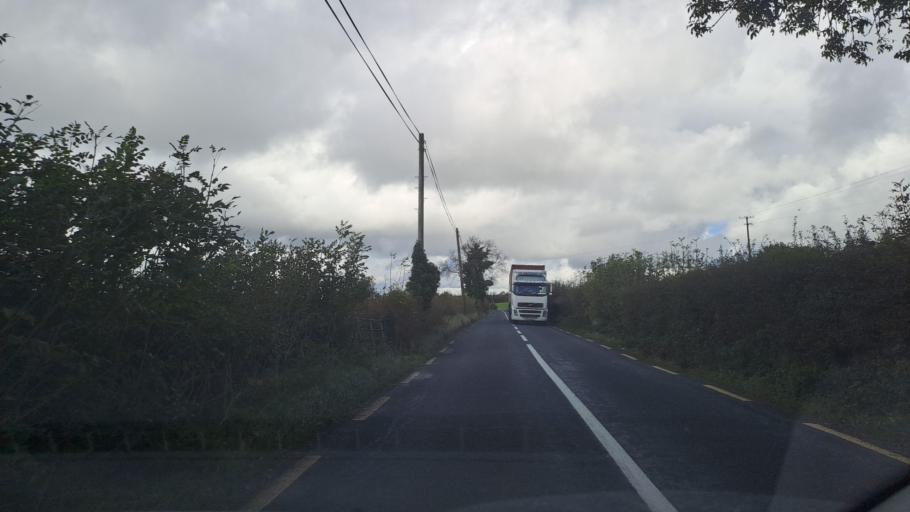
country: IE
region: Ulster
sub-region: An Cabhan
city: Bailieborough
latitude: 53.8715
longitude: -6.9653
